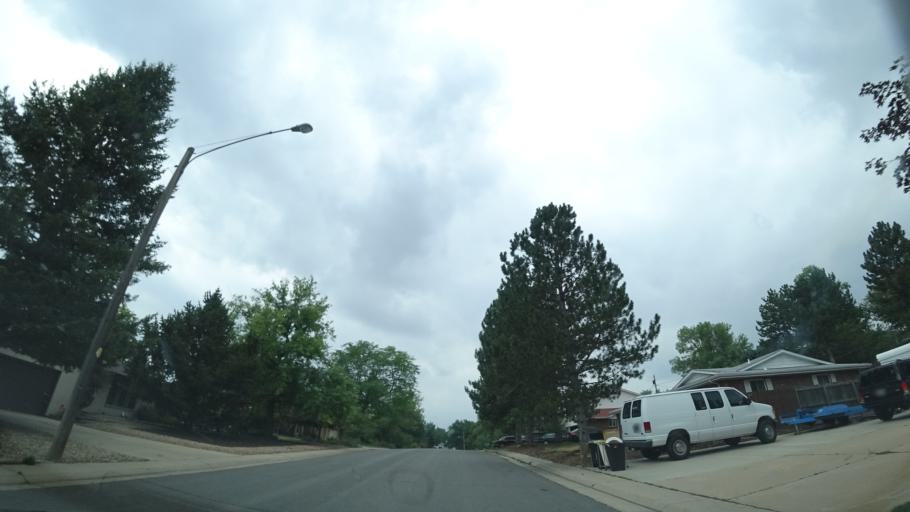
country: US
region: Colorado
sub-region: Jefferson County
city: West Pleasant View
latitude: 39.6995
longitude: -105.1487
